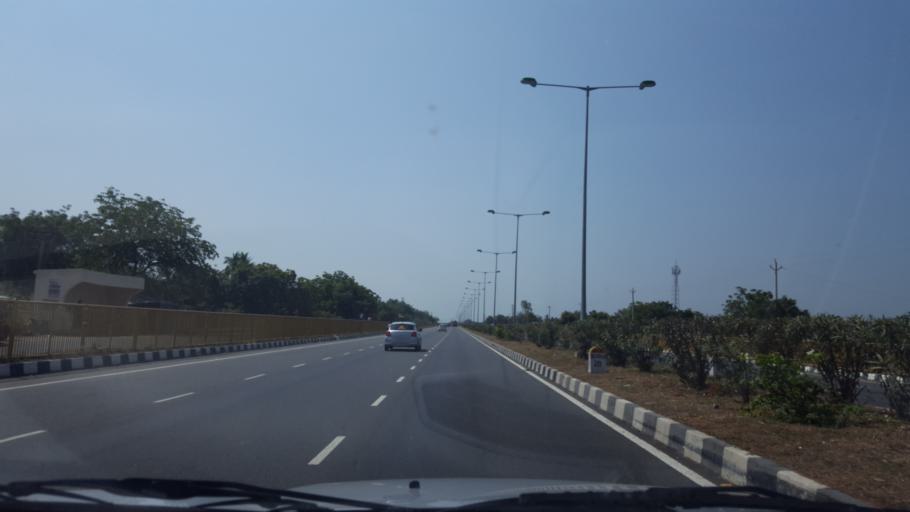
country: IN
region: Andhra Pradesh
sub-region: Prakasam
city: pedda nakkalapalem
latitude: 15.9632
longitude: 80.0923
